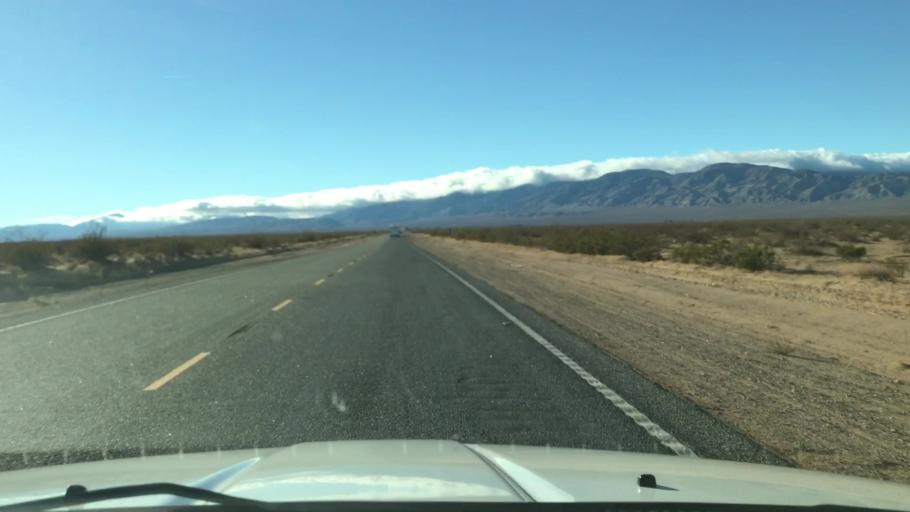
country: US
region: California
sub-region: Kern County
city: California City
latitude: 35.1255
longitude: -118.0514
